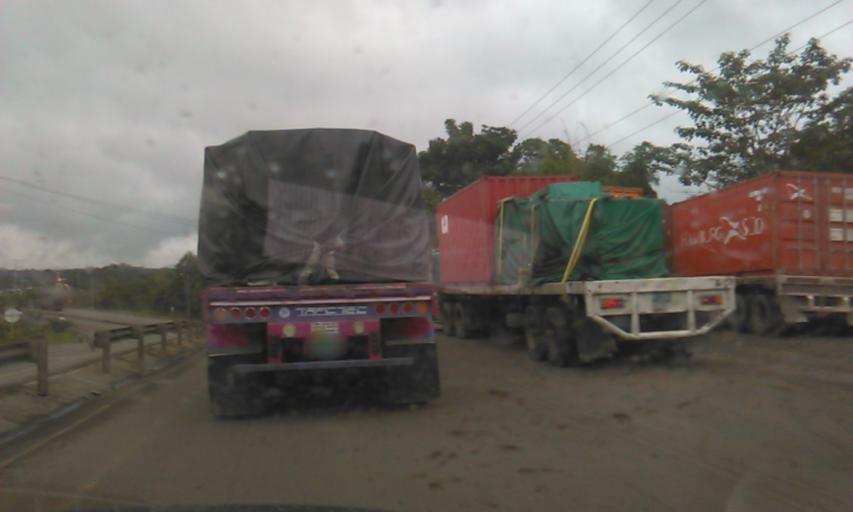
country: CO
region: Valle del Cauca
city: Buenaventura
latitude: 3.8774
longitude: -76.9071
